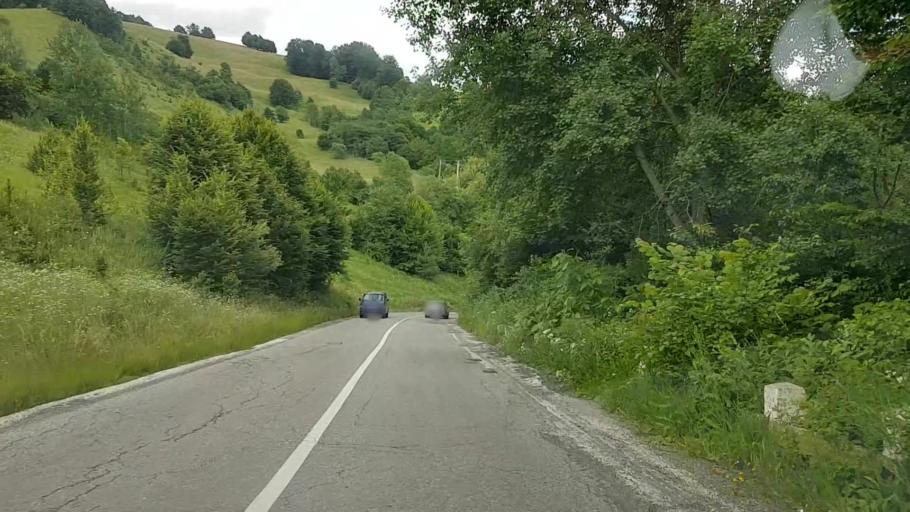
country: RO
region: Neamt
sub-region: Comuna Pangarati
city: Pangarati
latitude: 46.9546
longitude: 26.1238
